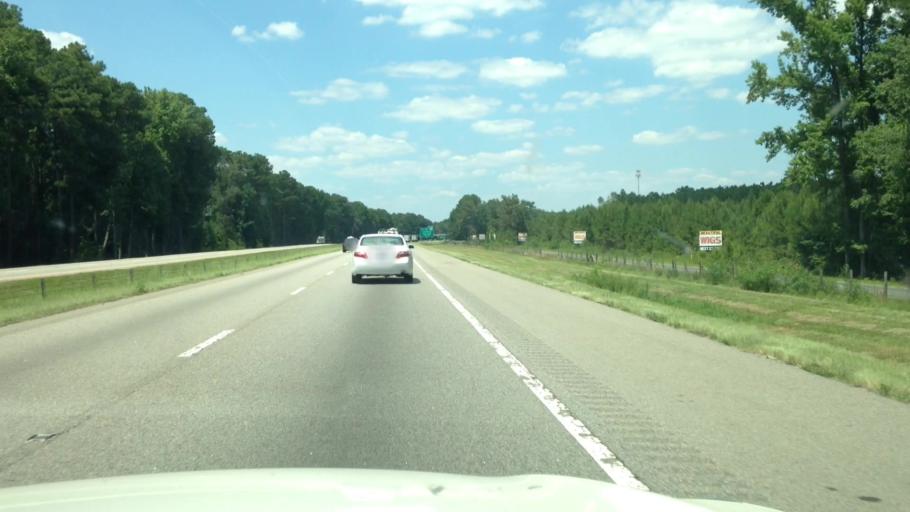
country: US
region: North Carolina
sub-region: Cumberland County
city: Hope Mills
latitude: 34.9003
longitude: -78.9581
